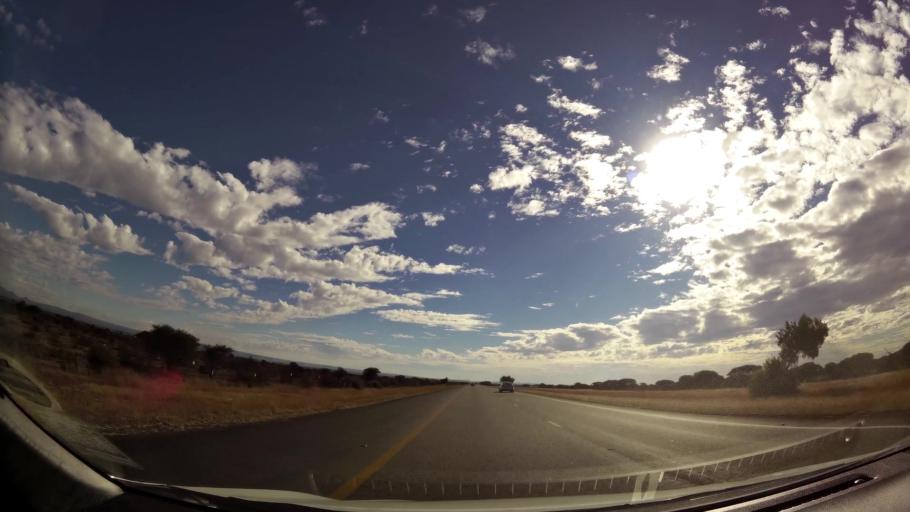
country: ZA
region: Limpopo
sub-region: Waterberg District Municipality
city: Bela-Bela
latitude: -25.0157
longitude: 28.3387
